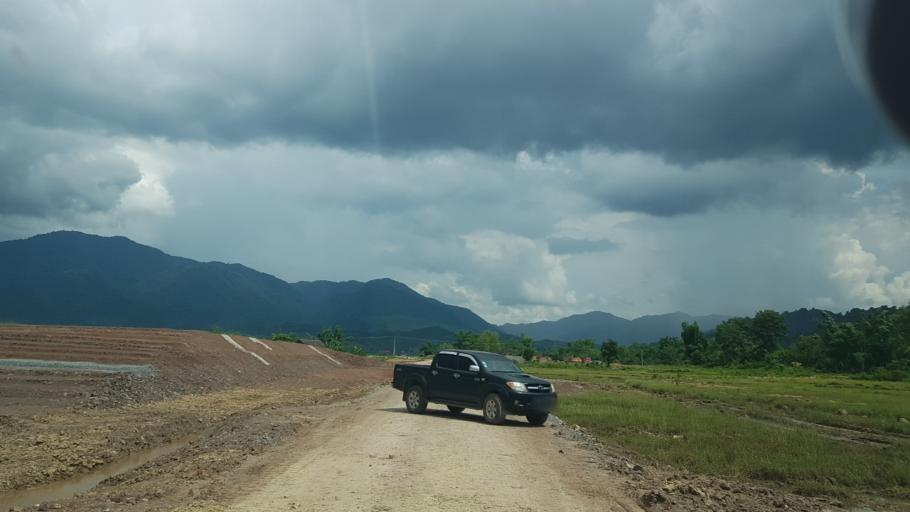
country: LA
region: Oudomxai
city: Muang Xay
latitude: 20.6801
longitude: 101.9689
